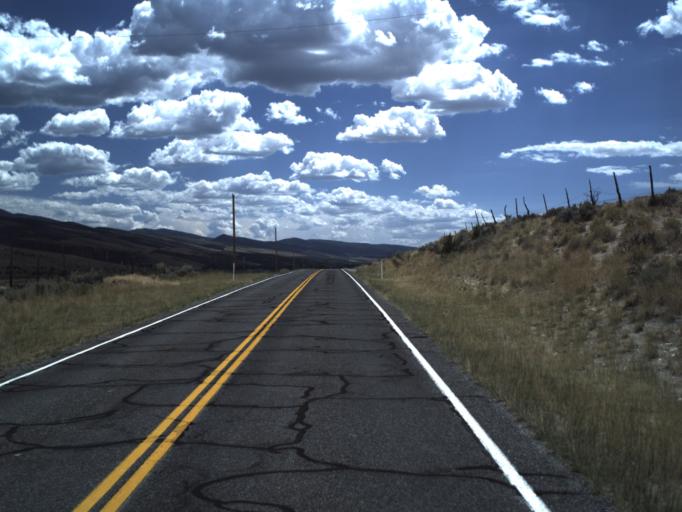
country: US
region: Utah
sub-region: Sanpete County
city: Gunnison
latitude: 39.1535
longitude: -111.7088
